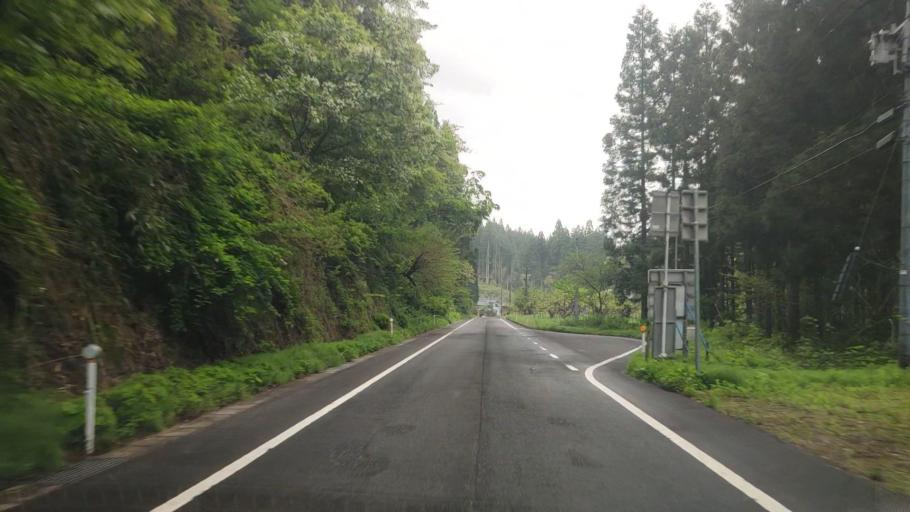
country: JP
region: Niigata
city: Gosen
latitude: 37.7189
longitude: 139.1268
